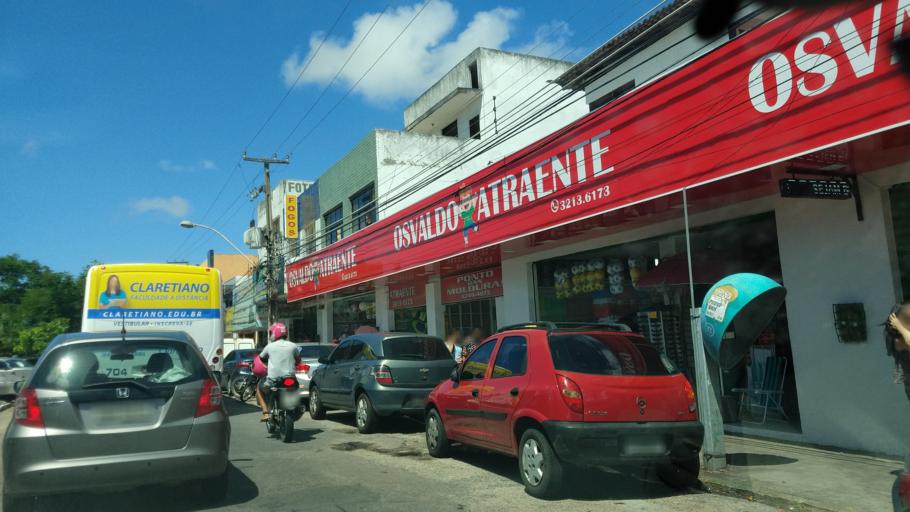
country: BR
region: Rio Grande do Norte
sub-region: Natal
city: Natal
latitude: -5.7987
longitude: -35.2169
